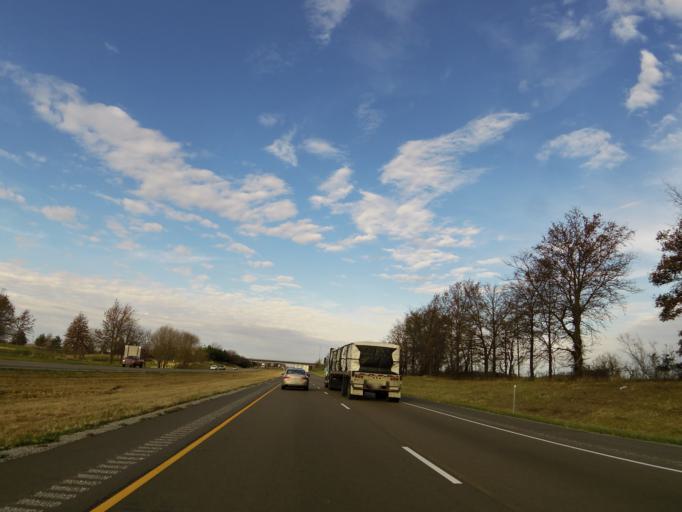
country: US
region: Illinois
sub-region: Washington County
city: Okawville
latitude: 38.4461
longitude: -89.5419
